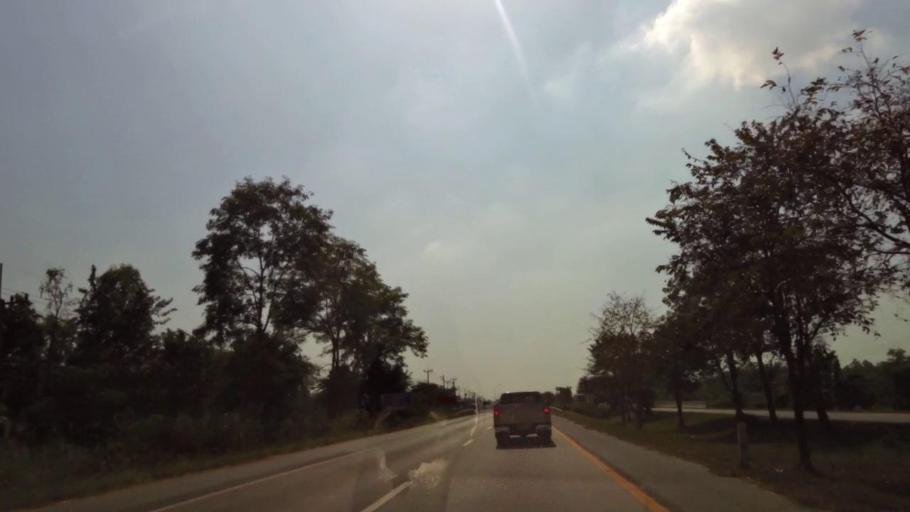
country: TH
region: Phichit
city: Wachira Barami
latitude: 16.5301
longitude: 100.1435
